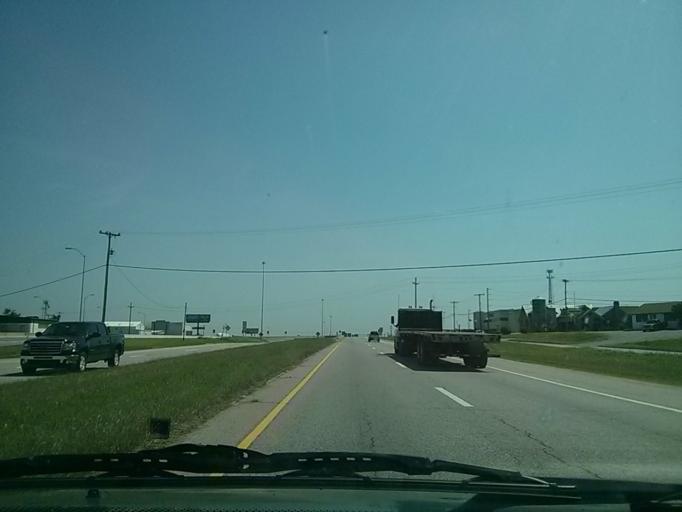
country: US
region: Oklahoma
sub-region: Tulsa County
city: Oakhurst
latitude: 36.0722
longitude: -96.0581
